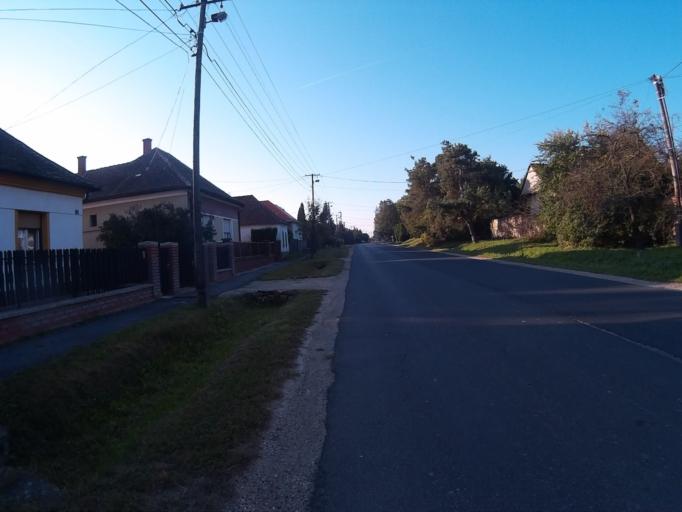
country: HU
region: Vas
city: Jak
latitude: 47.1371
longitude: 16.5836
